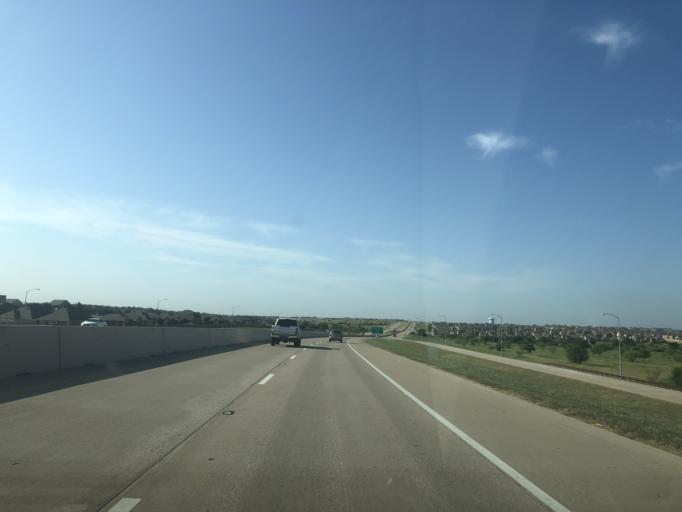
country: US
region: Texas
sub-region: Tarrant County
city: Benbrook
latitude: 32.6291
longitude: -97.4130
